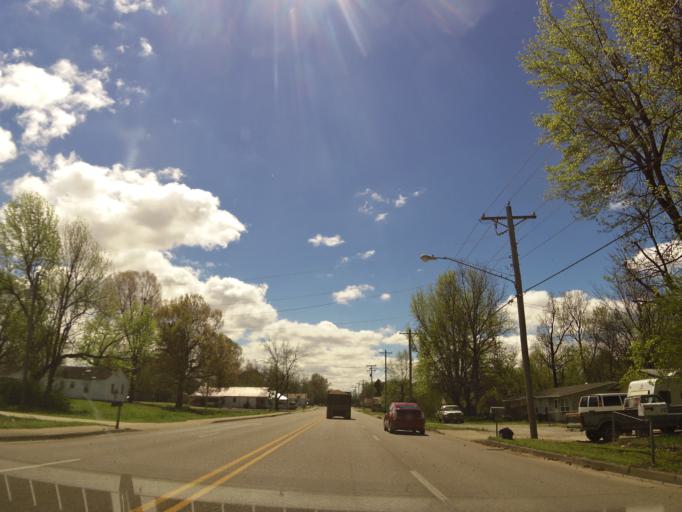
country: US
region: Arkansas
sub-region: Craighead County
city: Jonesboro
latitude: 35.8585
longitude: -90.7034
